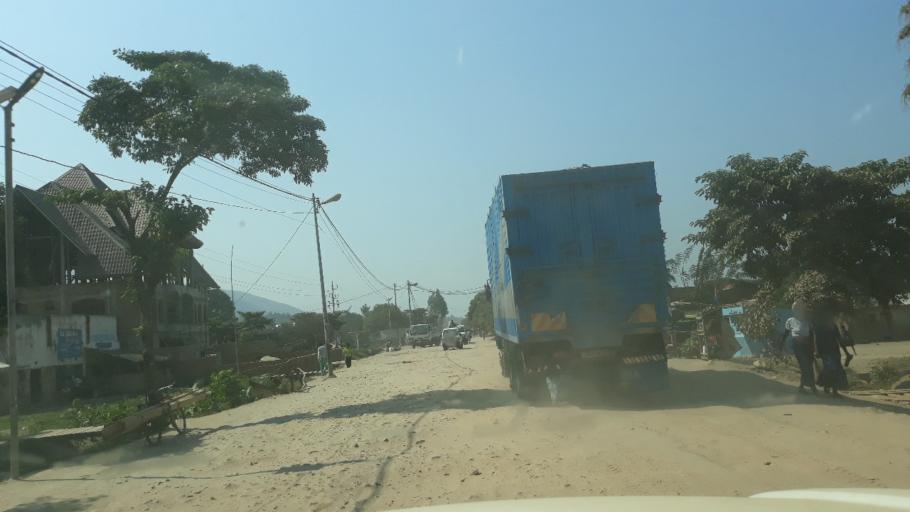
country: CD
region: South Kivu
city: Uvira
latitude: -3.3714
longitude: 29.1462
